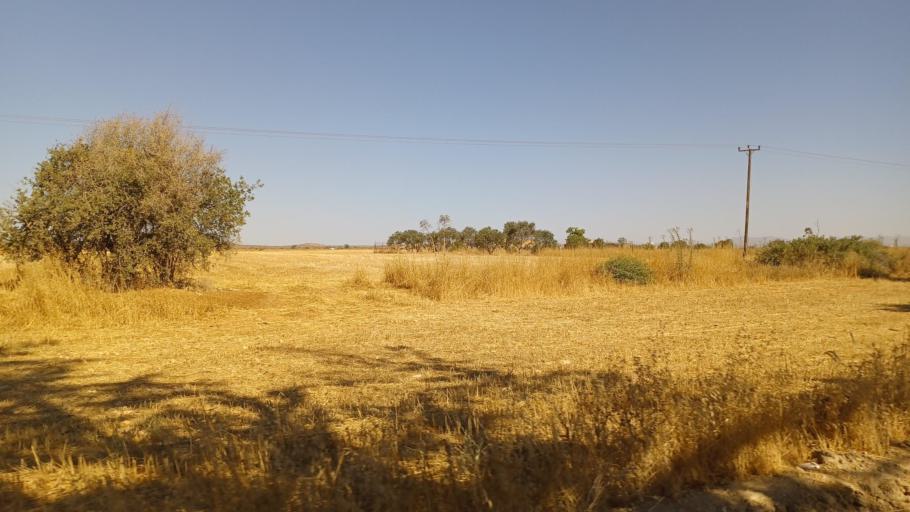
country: CY
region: Larnaka
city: Pergamos
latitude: 35.0447
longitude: 33.7039
